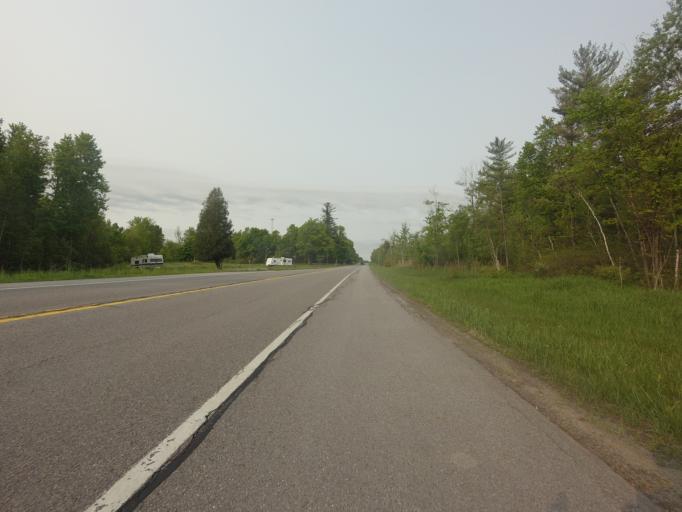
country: US
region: New York
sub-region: Jefferson County
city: Carthage
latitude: 44.0419
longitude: -75.5674
